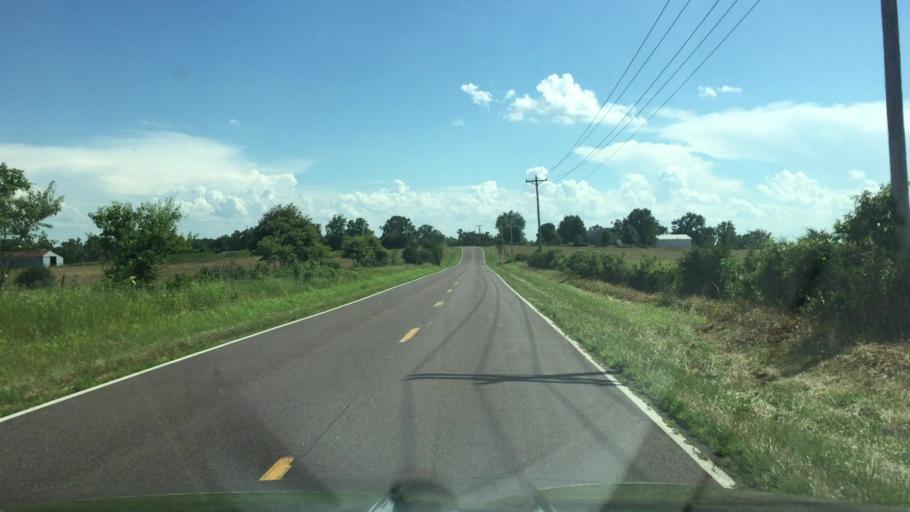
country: US
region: Missouri
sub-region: Miller County
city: Tuscumbia
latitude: 38.0992
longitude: -92.4781
